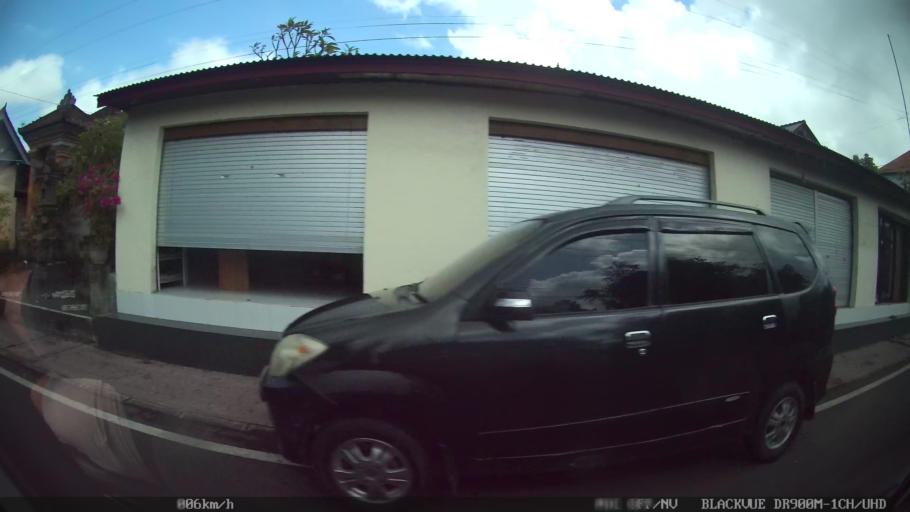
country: ID
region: Bali
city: Banjar Pasekan
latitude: -8.5938
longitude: 115.2844
